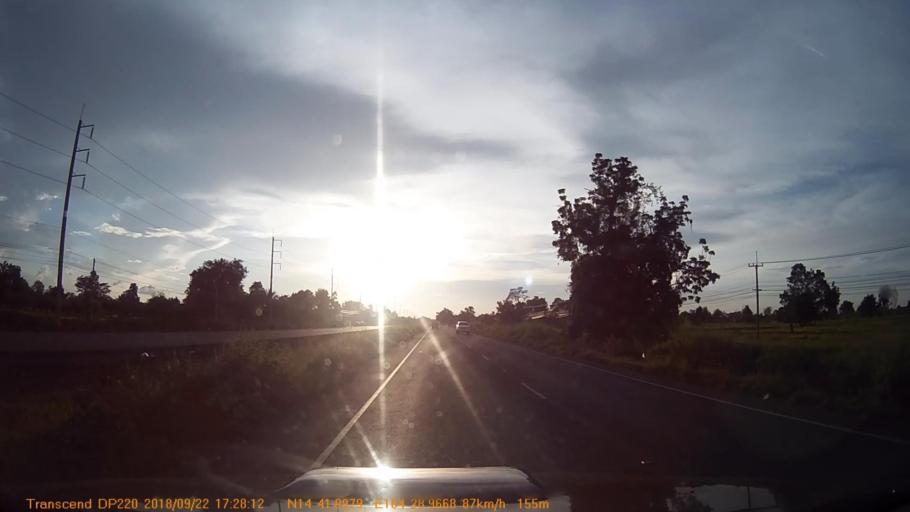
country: TH
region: Sisaket
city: Khun Han
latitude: 14.6855
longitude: 104.4823
